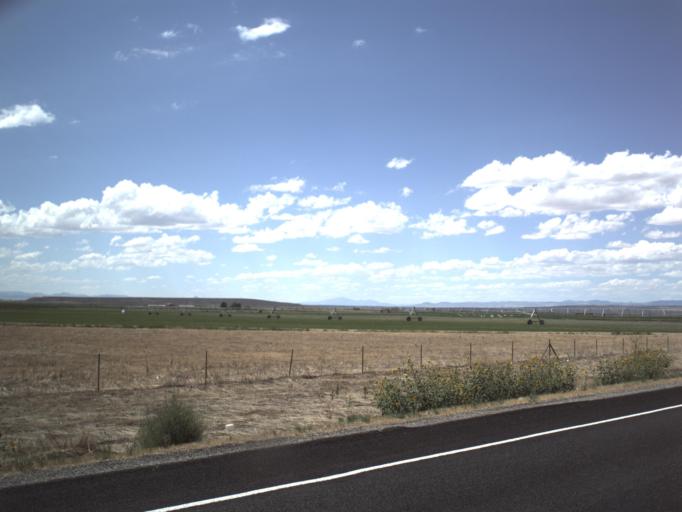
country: US
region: Utah
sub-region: Millard County
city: Fillmore
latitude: 39.1181
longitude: -112.3284
